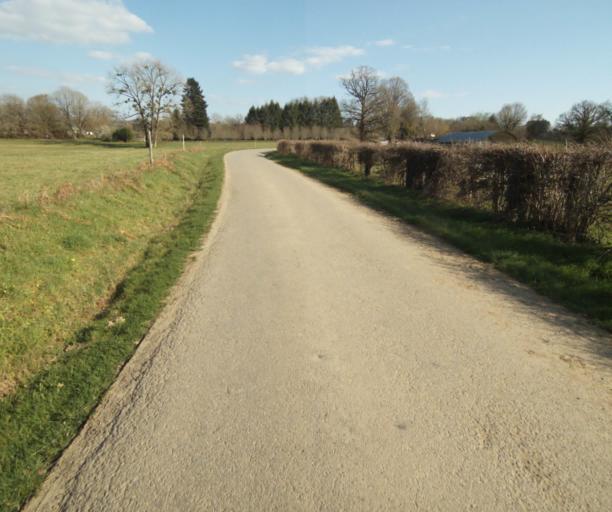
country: FR
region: Limousin
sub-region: Departement de la Correze
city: Saint-Mexant
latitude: 45.3395
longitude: 1.6068
